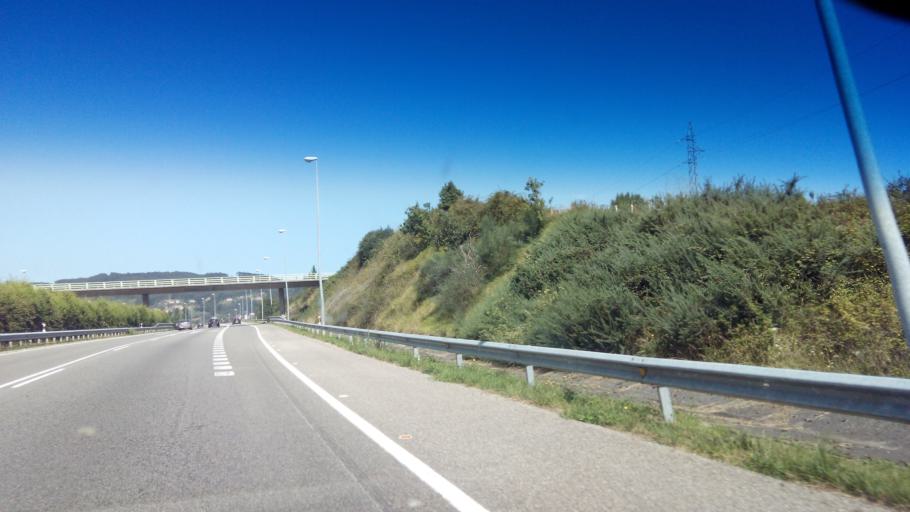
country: ES
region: Asturias
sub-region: Province of Asturias
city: Colunga
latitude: 43.4764
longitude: -5.2503
